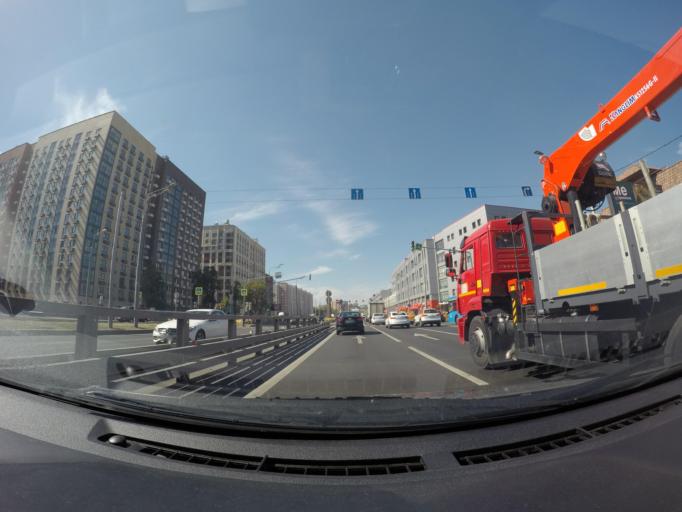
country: RU
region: Moscow
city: Lefortovo
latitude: 55.7325
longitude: 37.7153
